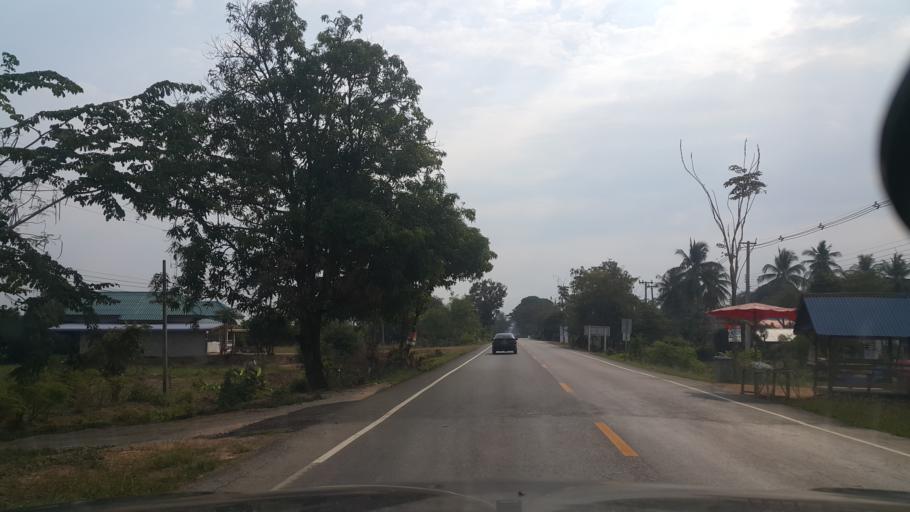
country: TH
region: Sukhothai
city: Si Samrong
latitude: 17.1802
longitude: 99.8392
